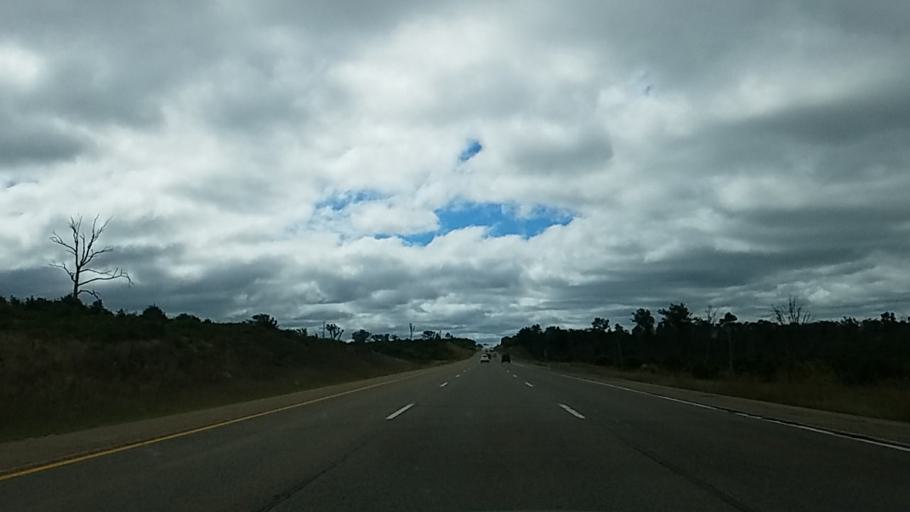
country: US
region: Michigan
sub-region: Crawford County
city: Grayling
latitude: 44.6350
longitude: -84.7089
